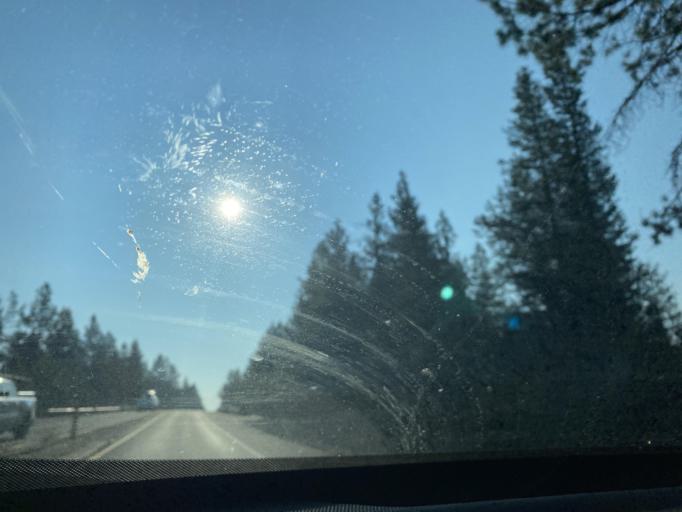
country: US
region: Oregon
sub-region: Deschutes County
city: Sunriver
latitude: 43.8693
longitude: -121.4320
